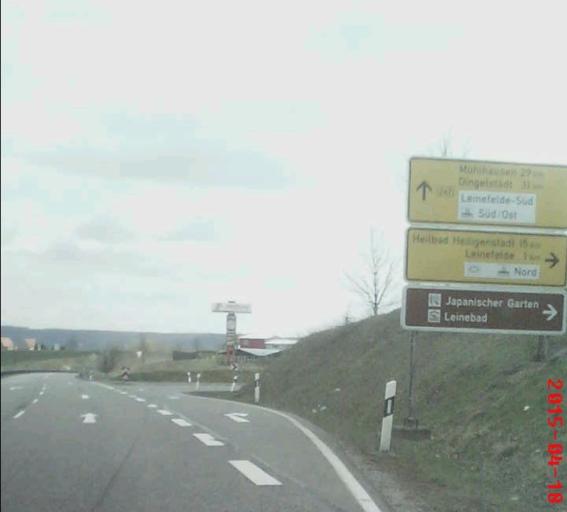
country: DE
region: Thuringia
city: Leinefelde
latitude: 51.3941
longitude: 10.3431
